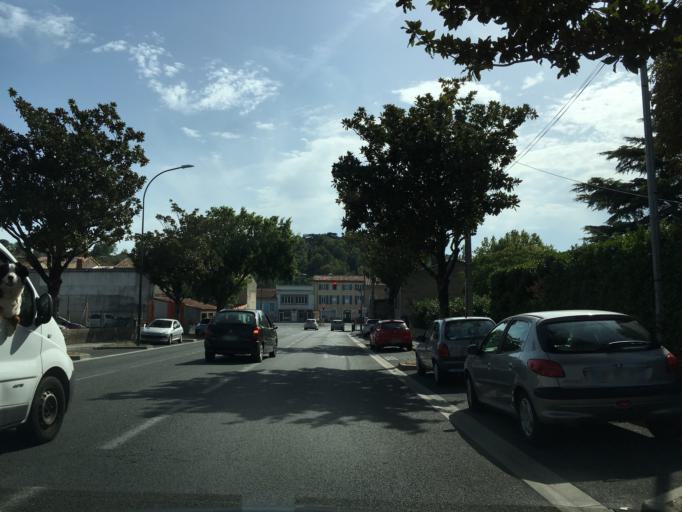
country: FR
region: Midi-Pyrenees
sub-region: Departement du Tarn
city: Castres
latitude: 43.6023
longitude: 2.2530
